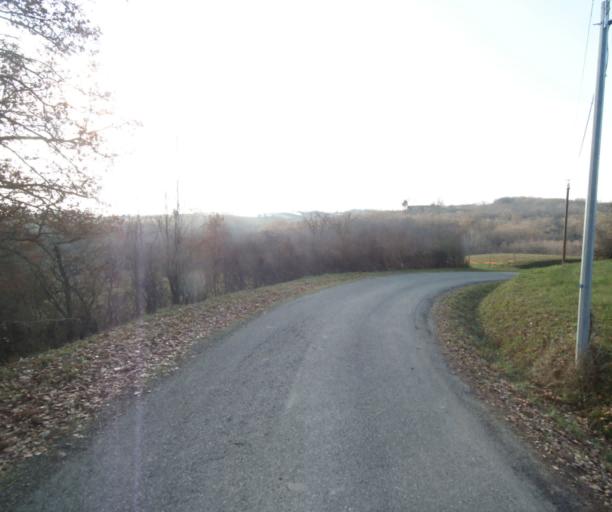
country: FR
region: Midi-Pyrenees
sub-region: Departement du Tarn-et-Garonne
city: Moissac
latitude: 44.1247
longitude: 1.0468
